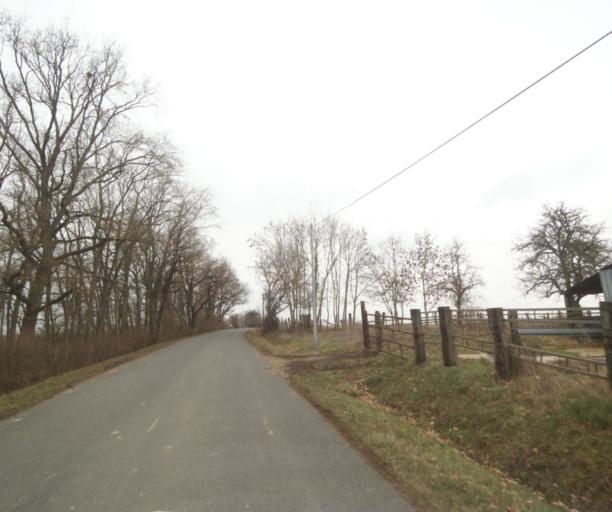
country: FR
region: Champagne-Ardenne
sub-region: Departement de la Marne
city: Pargny-sur-Saulx
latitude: 48.7435
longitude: 4.8420
